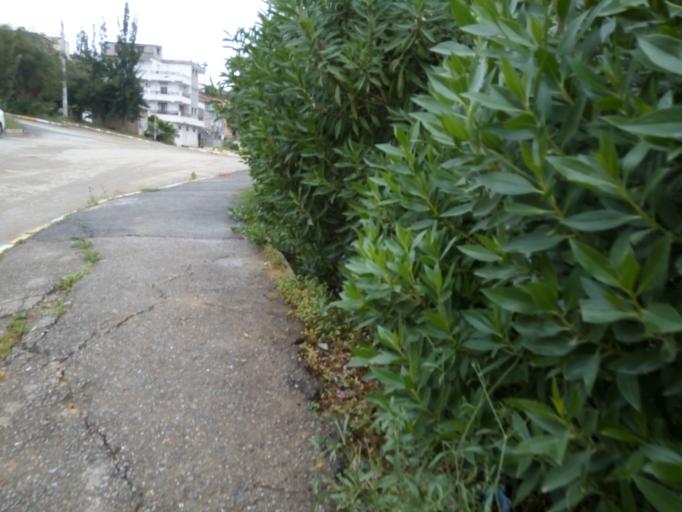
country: DZ
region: Tipaza
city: Douera
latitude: 36.6881
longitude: 2.9657
